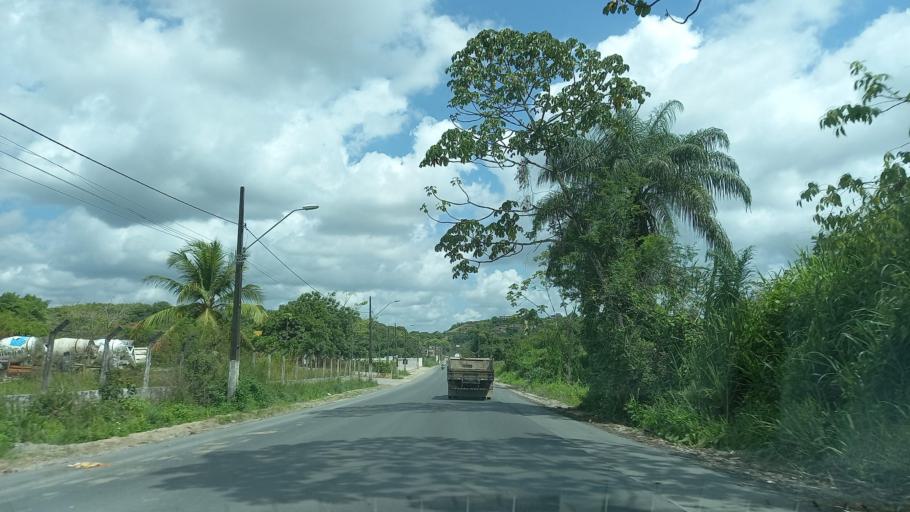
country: BR
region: Pernambuco
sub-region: Jaboatao Dos Guararapes
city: Jaboatao dos Guararapes
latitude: -8.1249
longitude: -35.0065
